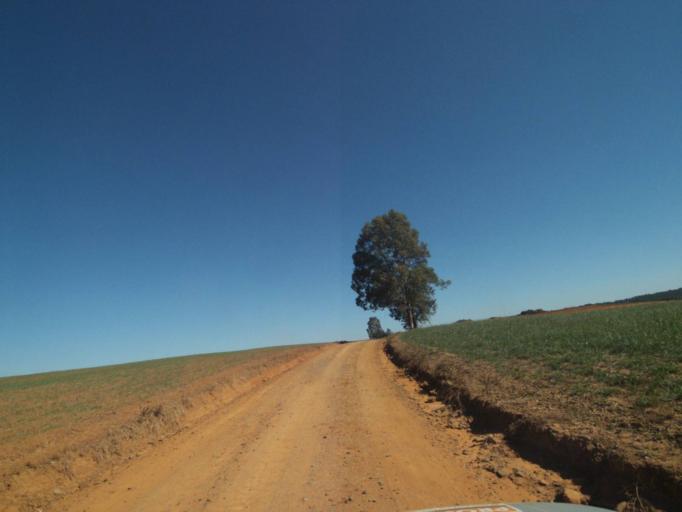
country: BR
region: Parana
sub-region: Tibagi
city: Tibagi
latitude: -24.5619
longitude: -50.6234
